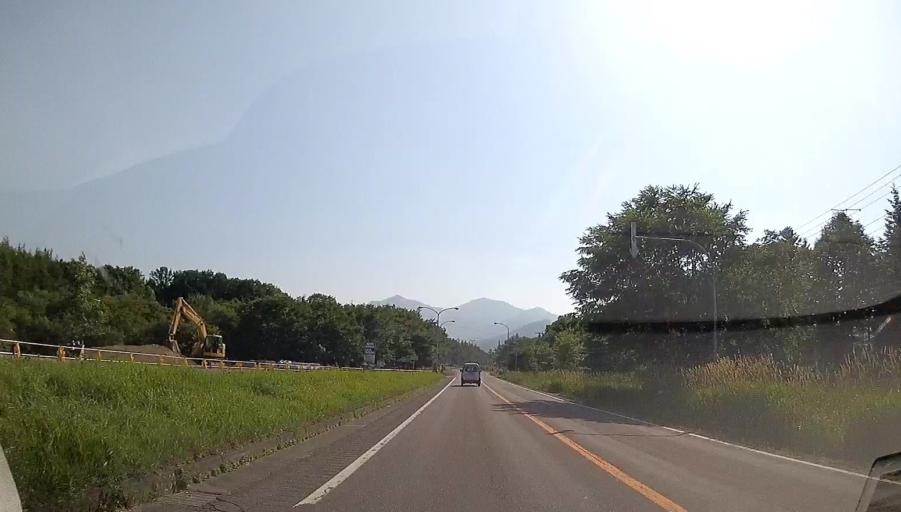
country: JP
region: Hokkaido
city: Otofuke
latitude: 42.9896
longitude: 142.8426
